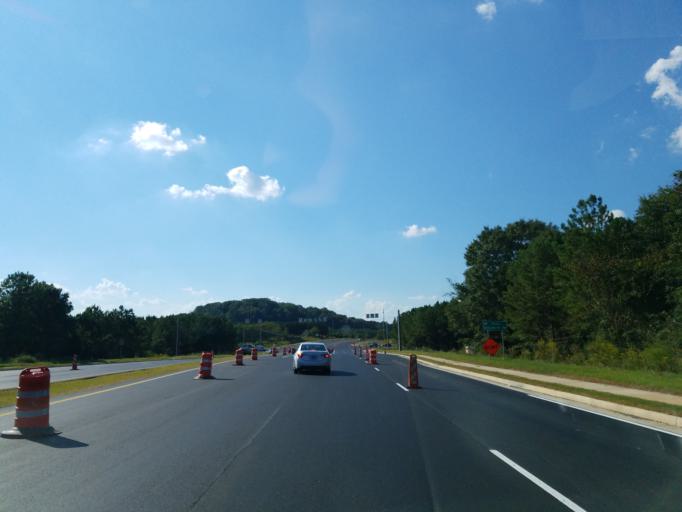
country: US
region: Georgia
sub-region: Bartow County
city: Cartersville
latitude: 34.2073
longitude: -84.7964
